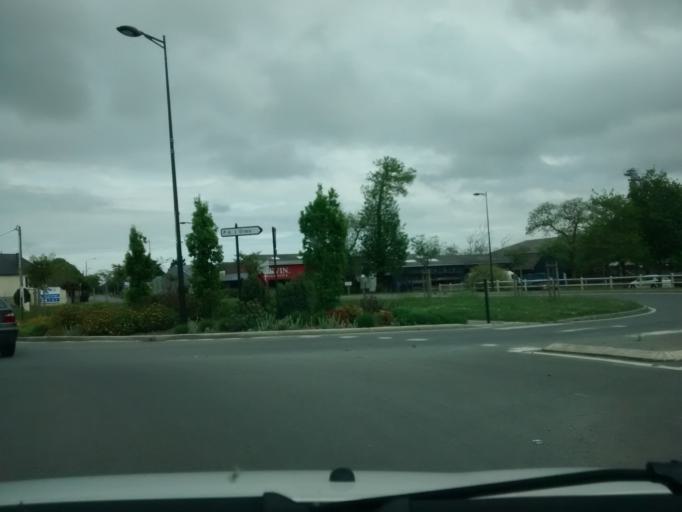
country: FR
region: Brittany
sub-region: Departement d'Ille-et-Vilaine
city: Pleurtuit
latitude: 48.5714
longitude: -2.0592
